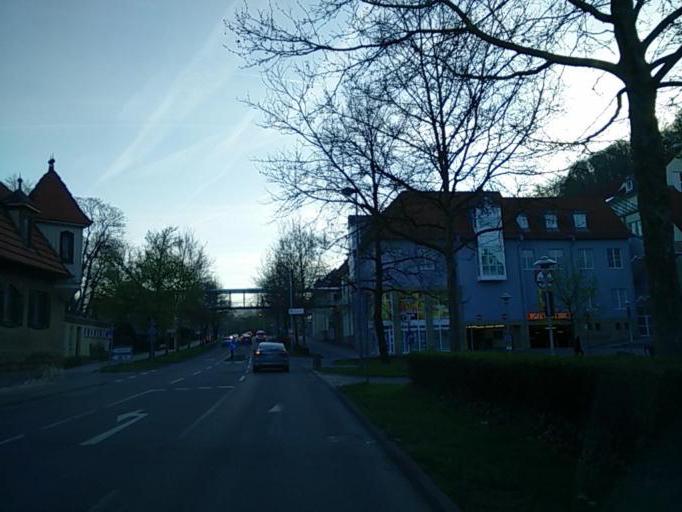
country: DE
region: Baden-Wuerttemberg
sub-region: Regierungsbezirk Stuttgart
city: Herrenberg
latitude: 48.5978
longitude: 8.8695
